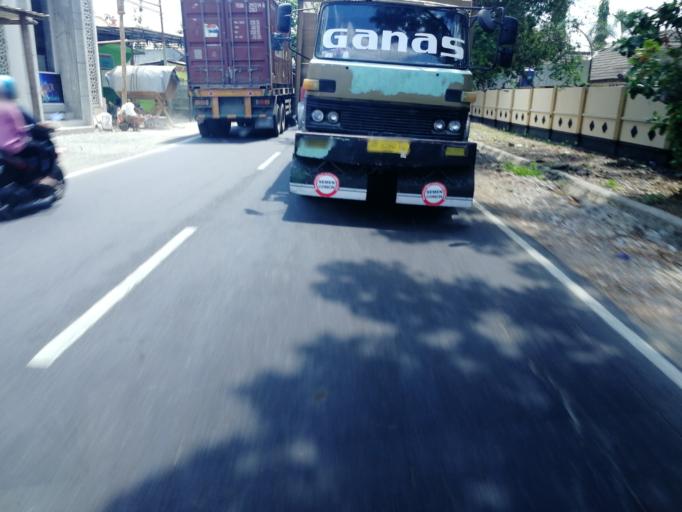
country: ID
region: West Nusa Tenggara
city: Jelateng Timur
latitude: -8.7048
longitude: 116.0885
